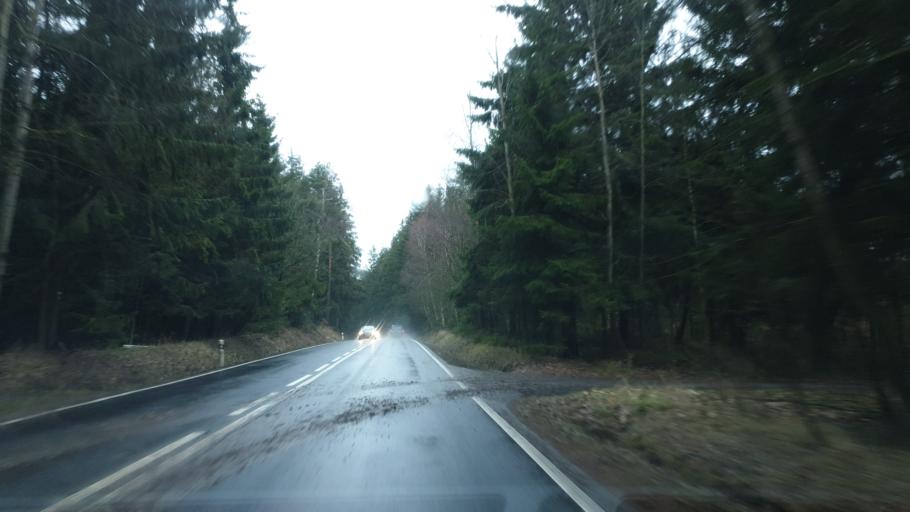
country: CZ
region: Karlovarsky
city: As
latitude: 50.2616
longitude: 12.1845
